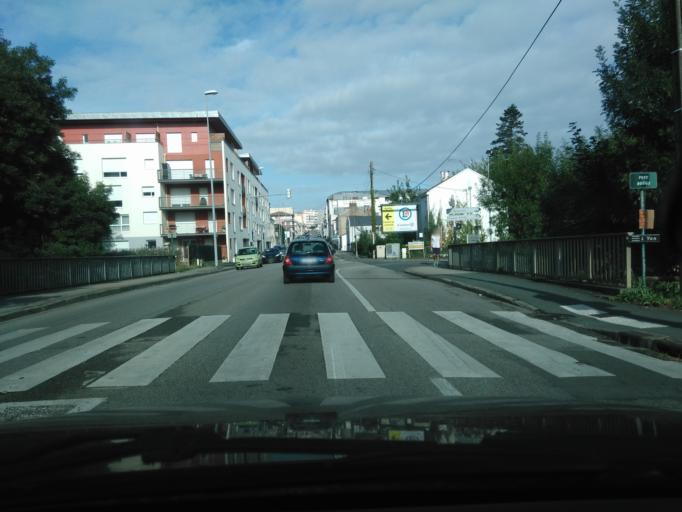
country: FR
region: Pays de la Loire
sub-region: Departement de la Vendee
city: La Roche-sur-Yon
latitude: 46.6706
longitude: -1.4152
